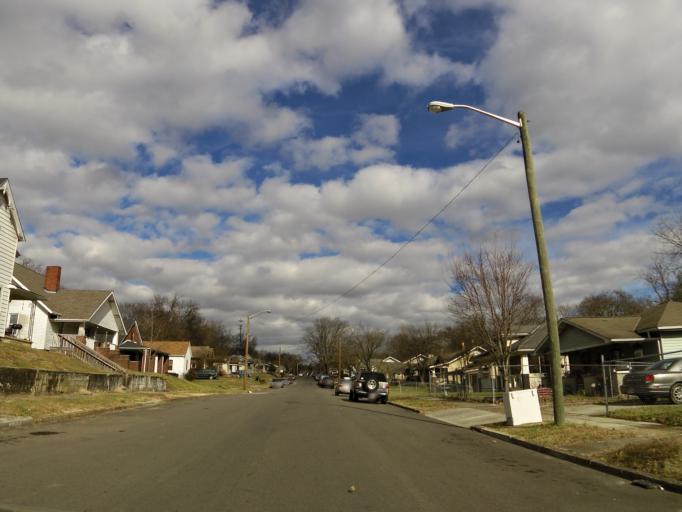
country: US
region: Tennessee
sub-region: Knox County
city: Knoxville
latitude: 35.9858
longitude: -83.9041
